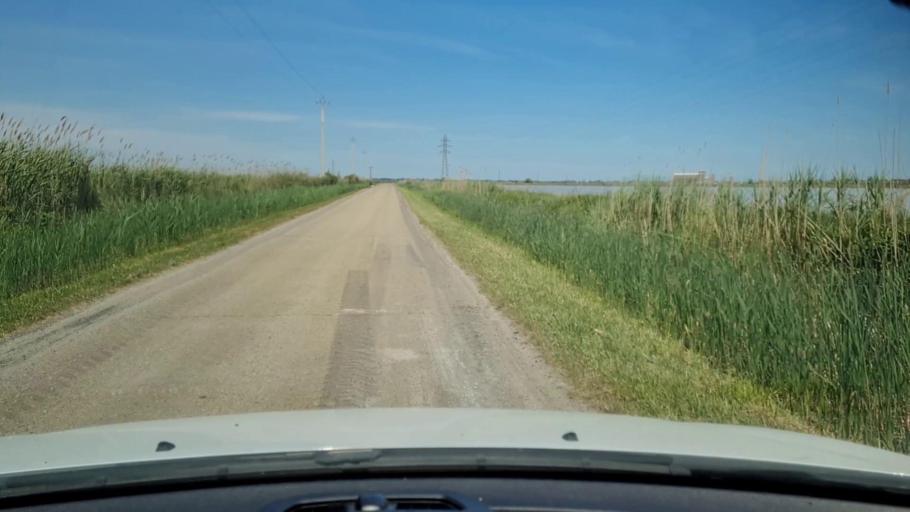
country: FR
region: Languedoc-Roussillon
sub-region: Departement du Gard
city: Saint-Gilles
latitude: 43.5765
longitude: 4.3973
